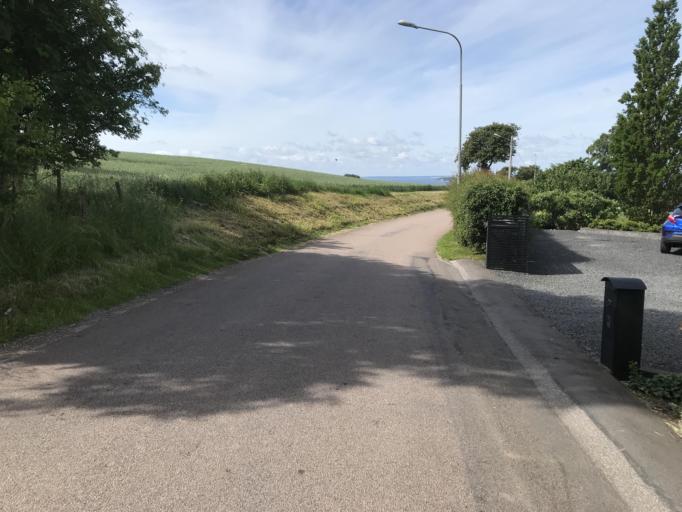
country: SE
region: Skane
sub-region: Helsingborg
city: Glumslov
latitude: 55.9342
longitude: 12.8002
